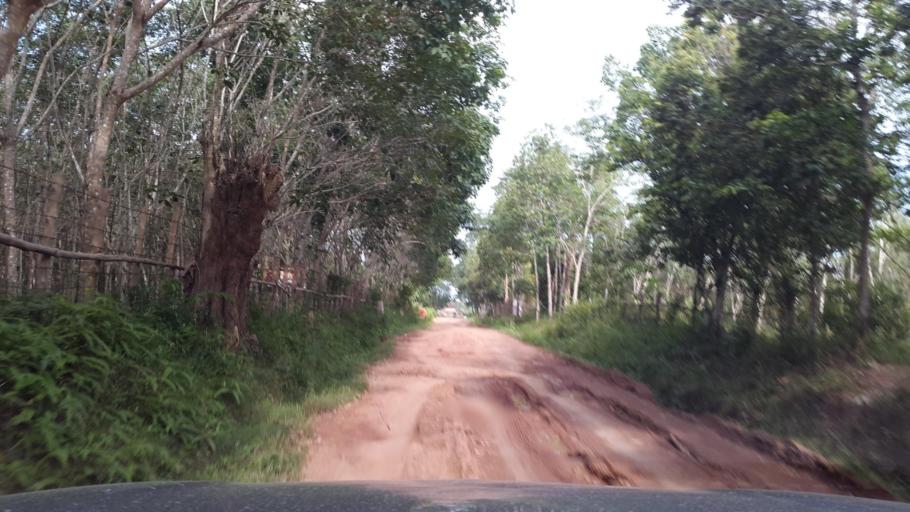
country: ID
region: South Sumatra
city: Glumbang
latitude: -3.4233
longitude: 104.4569
